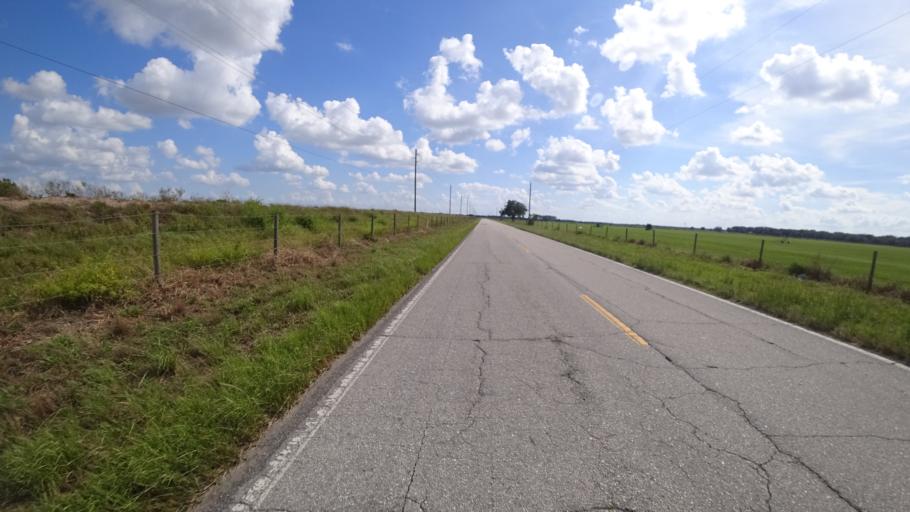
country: US
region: Florida
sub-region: Hardee County
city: Wauchula
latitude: 27.5265
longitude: -82.0756
